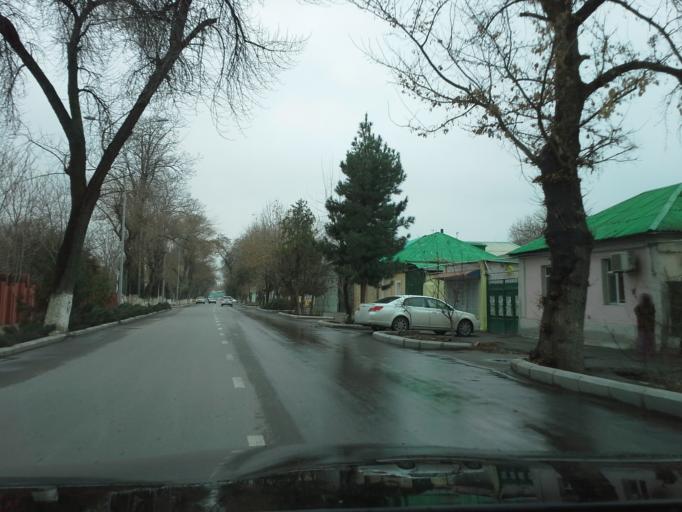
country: TM
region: Ahal
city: Ashgabat
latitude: 37.9530
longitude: 58.3641
